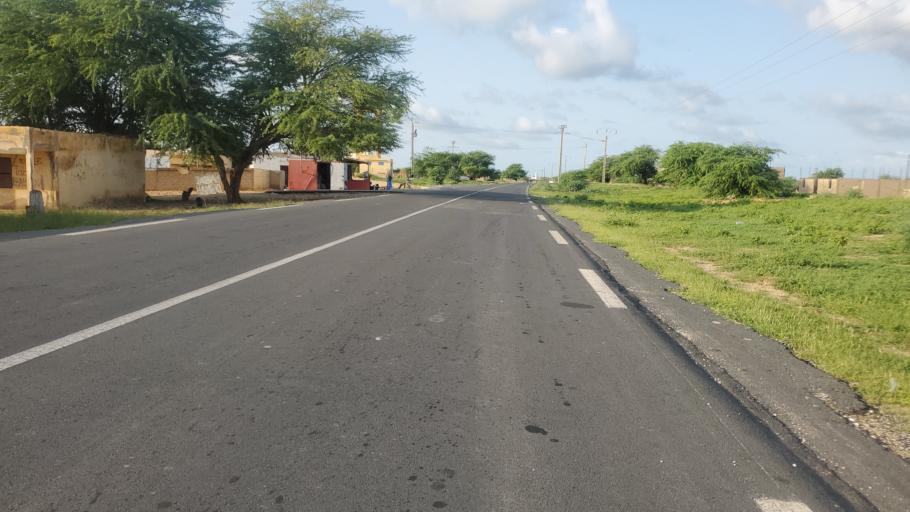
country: SN
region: Saint-Louis
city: Saint-Louis
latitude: 16.1352
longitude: -16.4115
